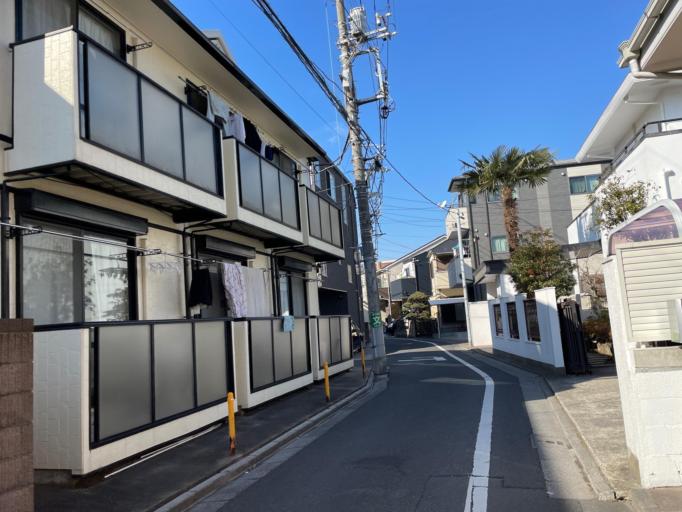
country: JP
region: Saitama
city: Soka
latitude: 35.7757
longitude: 139.7793
